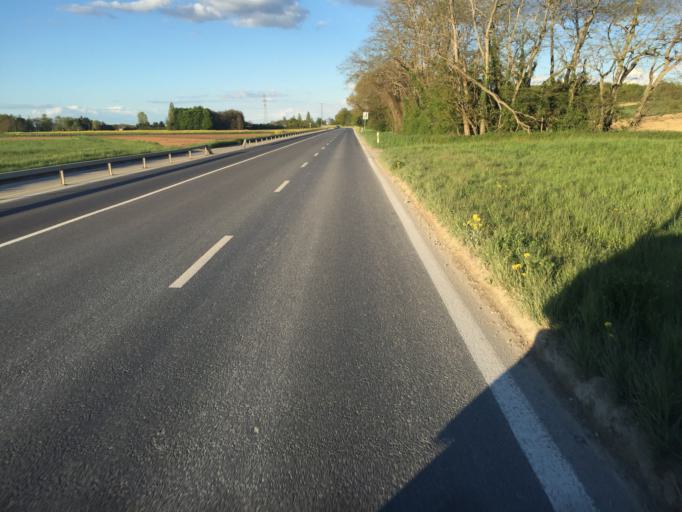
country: CH
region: Geneva
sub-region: Geneva
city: Aire-la-Ville
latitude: 46.1672
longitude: 6.0291
